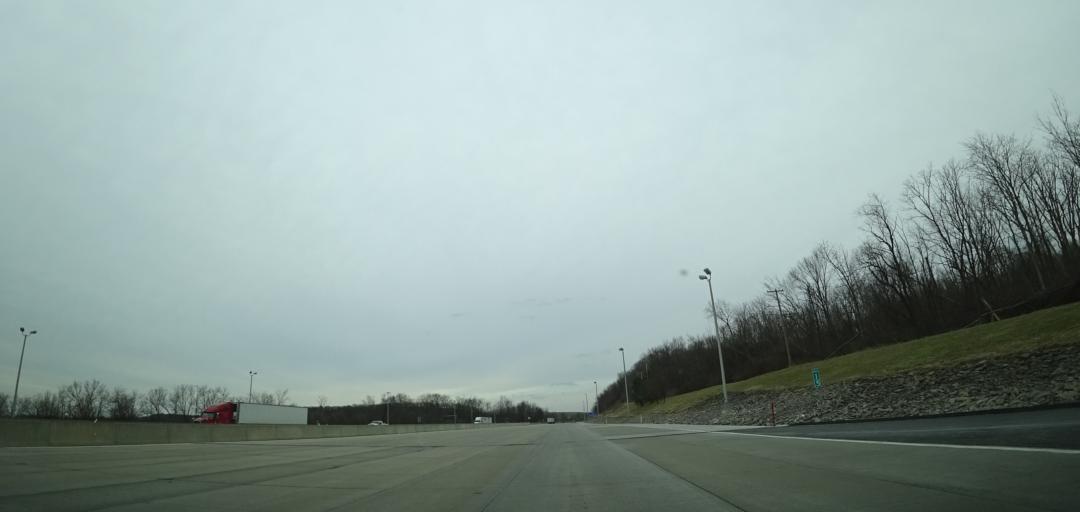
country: US
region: Pennsylvania
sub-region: Lawrence County
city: Bessemer
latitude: 40.9038
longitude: -80.4942
